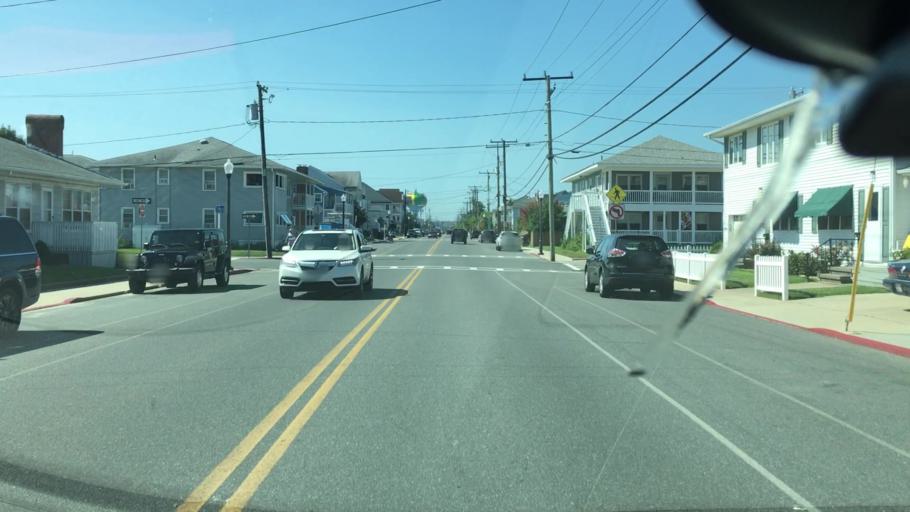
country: US
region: Maryland
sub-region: Worcester County
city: Ocean City
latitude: 38.3410
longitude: -75.0839
